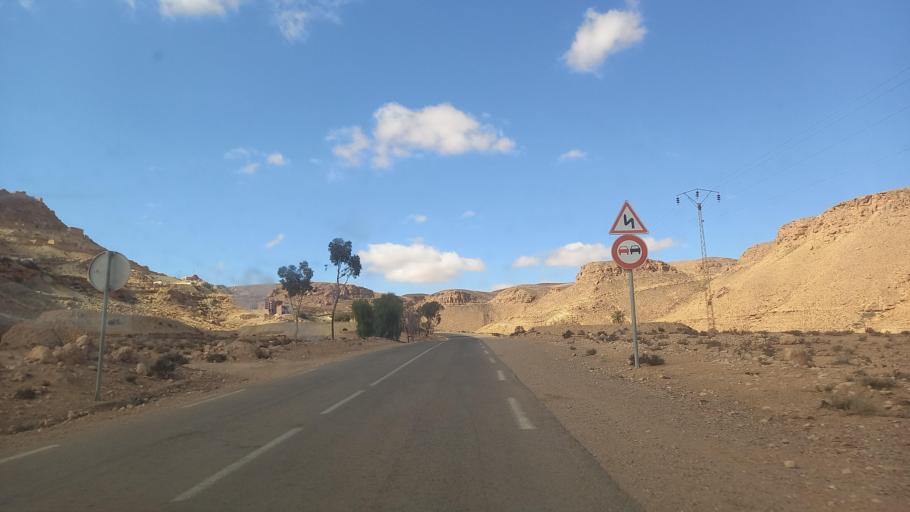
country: TN
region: Tataouine
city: Tataouine
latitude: 32.9166
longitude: 10.2653
